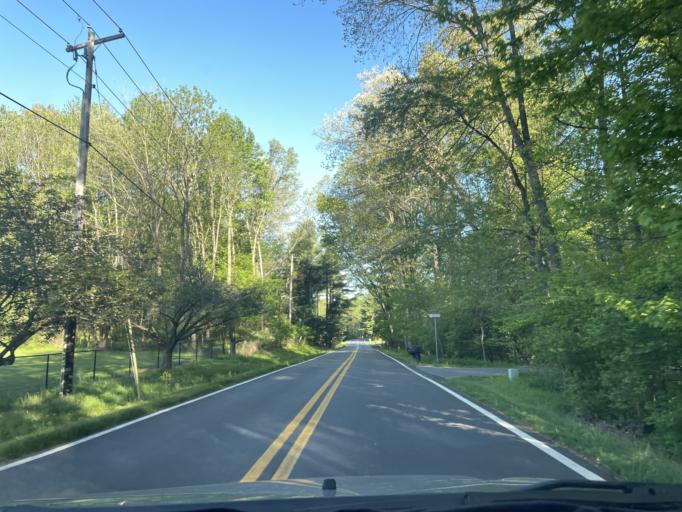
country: US
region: Maryland
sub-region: Carroll County
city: Mount Airy
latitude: 39.4112
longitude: -77.1337
